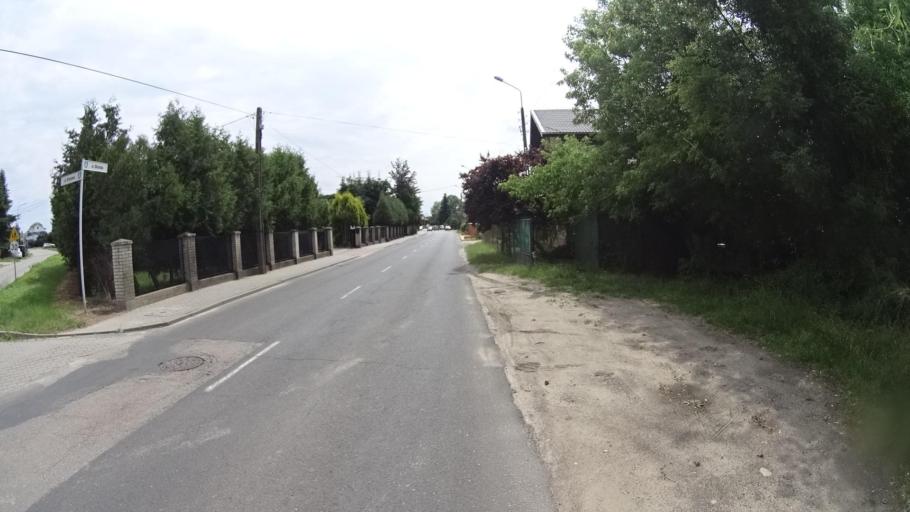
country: PL
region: Masovian Voivodeship
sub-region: Powiat piaseczynski
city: Tarczyn
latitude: 51.9832
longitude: 20.8305
